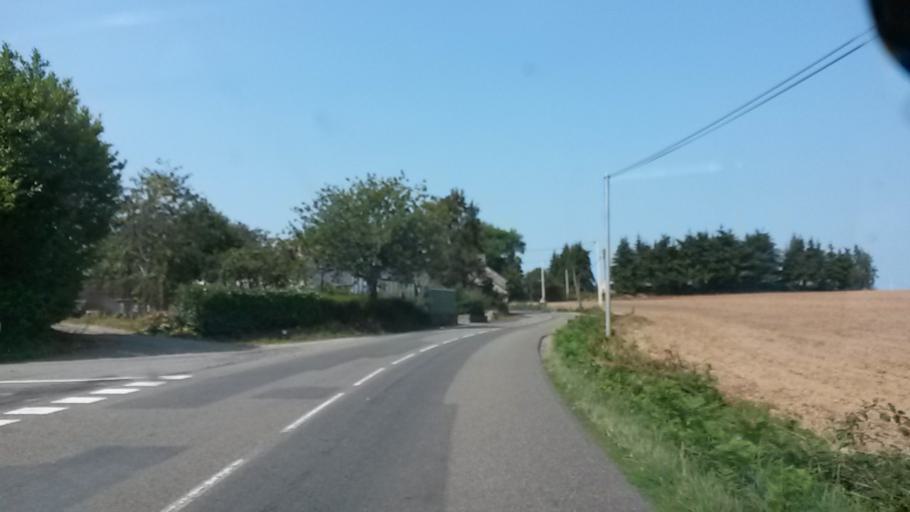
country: FR
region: Pays de la Loire
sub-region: Departement de la Mayenne
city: Saint-Pierre-des-Nids
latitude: 48.3708
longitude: -0.1801
